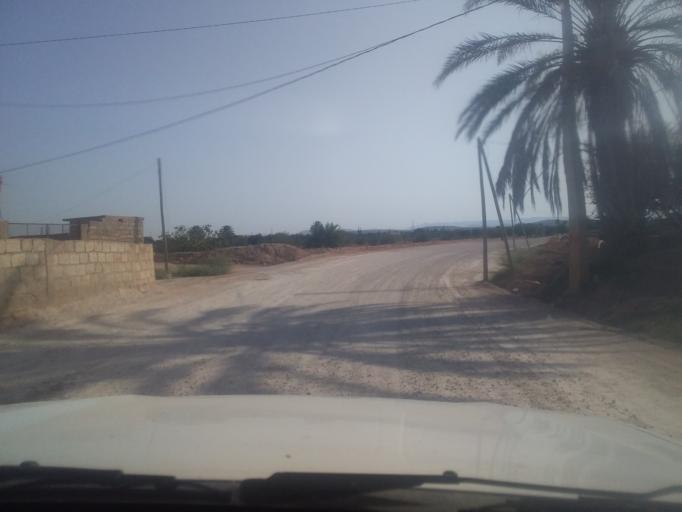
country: TN
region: Qabis
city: Matmata
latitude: 33.5996
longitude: 10.2754
